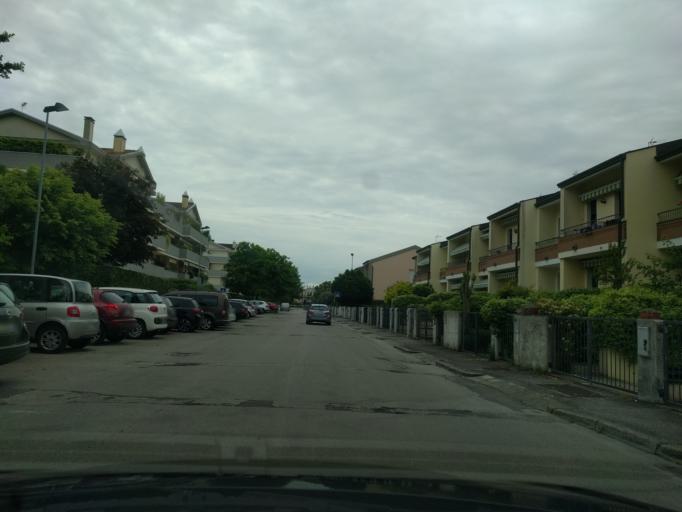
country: IT
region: Veneto
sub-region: Provincia di Rovigo
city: Rovigo
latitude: 45.0615
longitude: 11.7874
